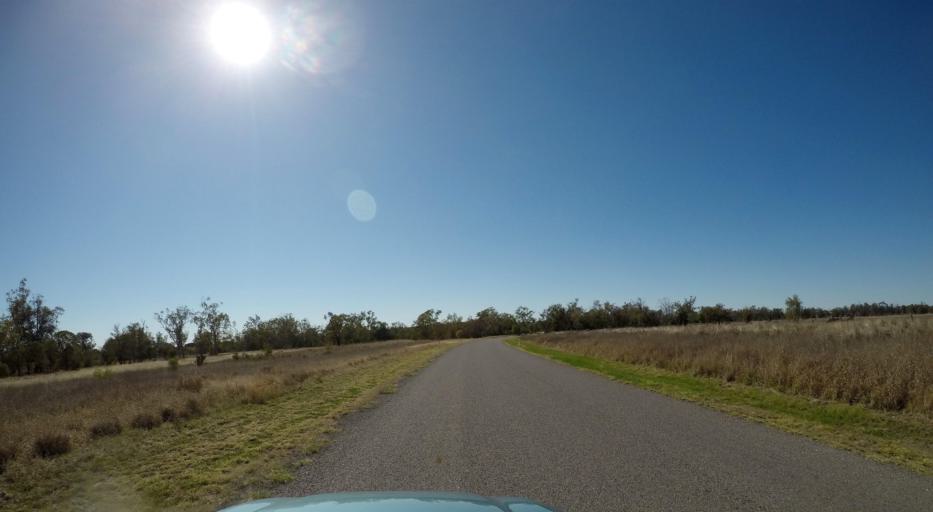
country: AU
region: Queensland
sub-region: Banana
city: Taroom
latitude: -25.7871
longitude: 149.6700
